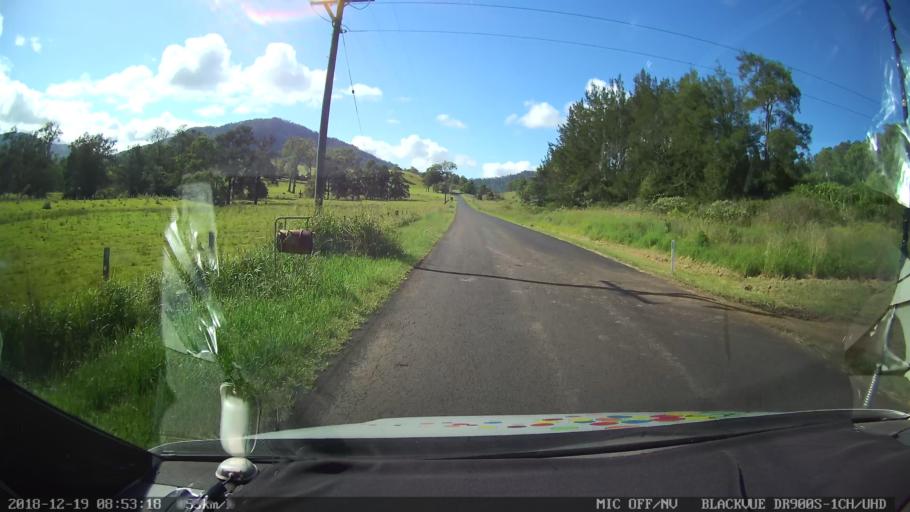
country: AU
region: New South Wales
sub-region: Kyogle
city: Kyogle
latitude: -28.3996
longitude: 152.9766
